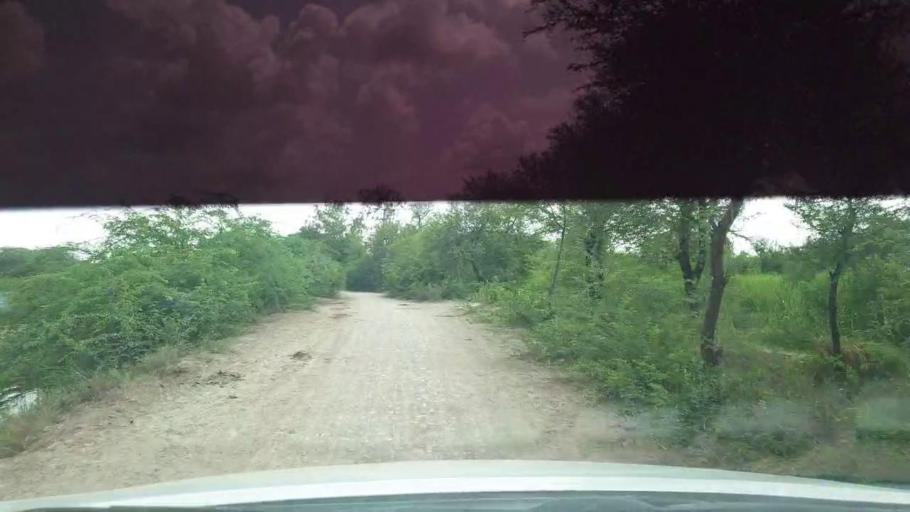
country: PK
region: Sindh
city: Kadhan
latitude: 24.6175
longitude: 69.0285
